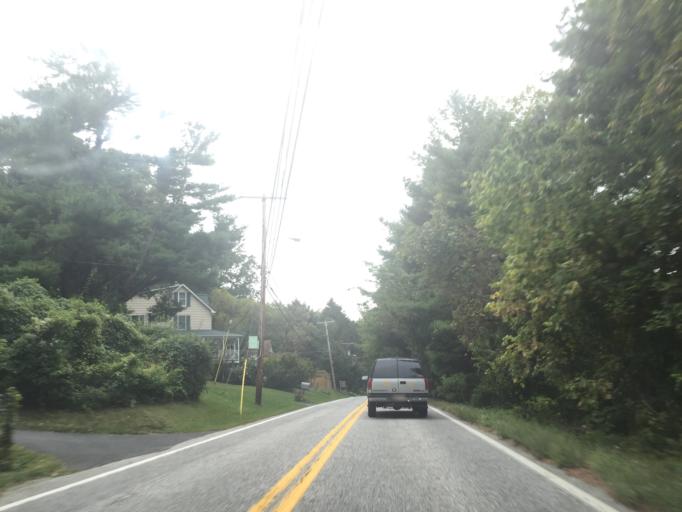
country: US
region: Maryland
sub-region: Baltimore County
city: Perry Hall
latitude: 39.4546
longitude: -76.4896
